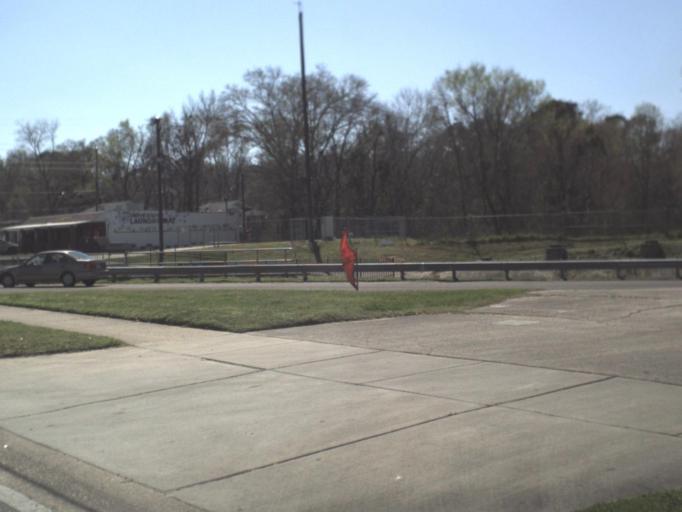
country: US
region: Florida
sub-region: Leon County
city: Tallahassee
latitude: 30.4303
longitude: -84.3023
